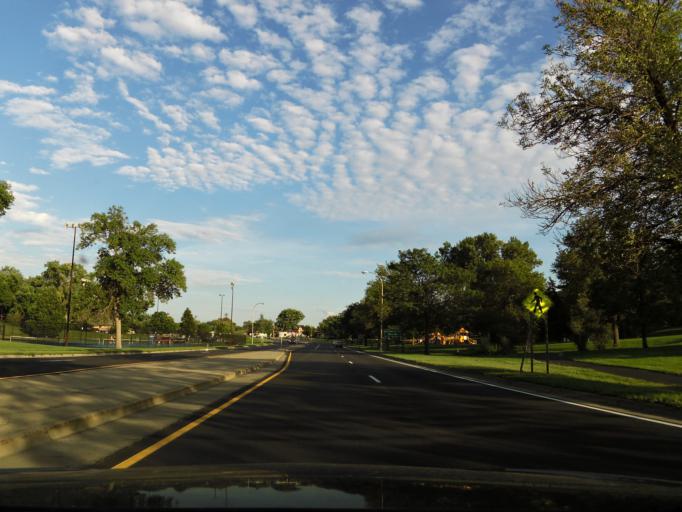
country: US
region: Minnesota
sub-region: Dakota County
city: Hastings
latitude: 44.7372
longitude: -92.8589
